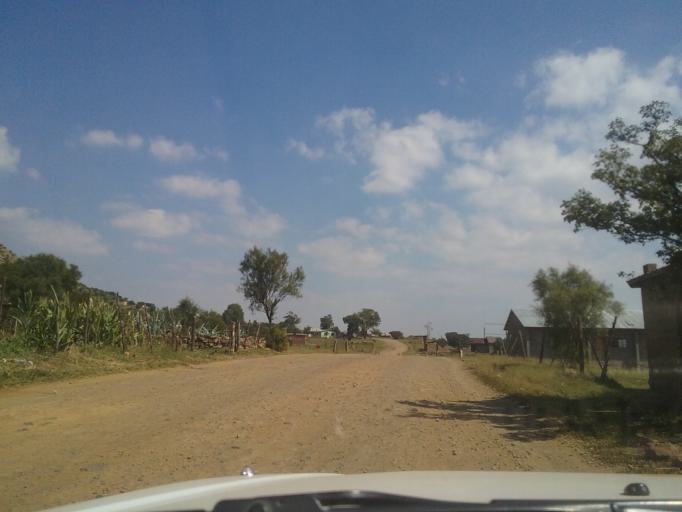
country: LS
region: Maseru
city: Maseru
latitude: -29.3999
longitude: 27.4440
